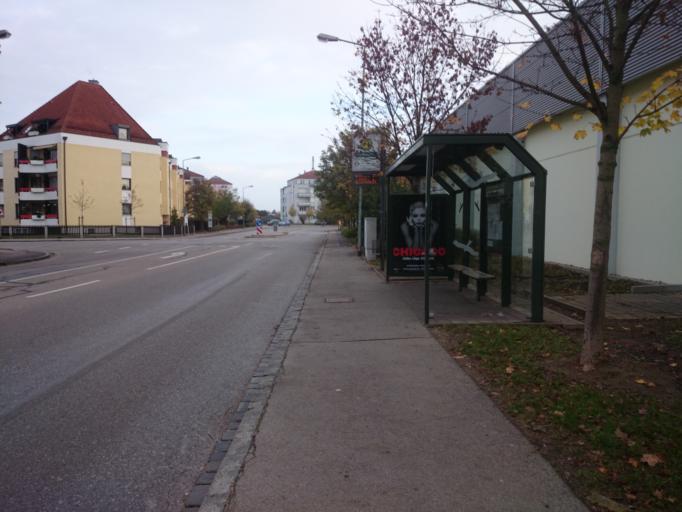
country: DE
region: Bavaria
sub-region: Swabia
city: Konigsbrunn
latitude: 48.2971
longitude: 10.8985
